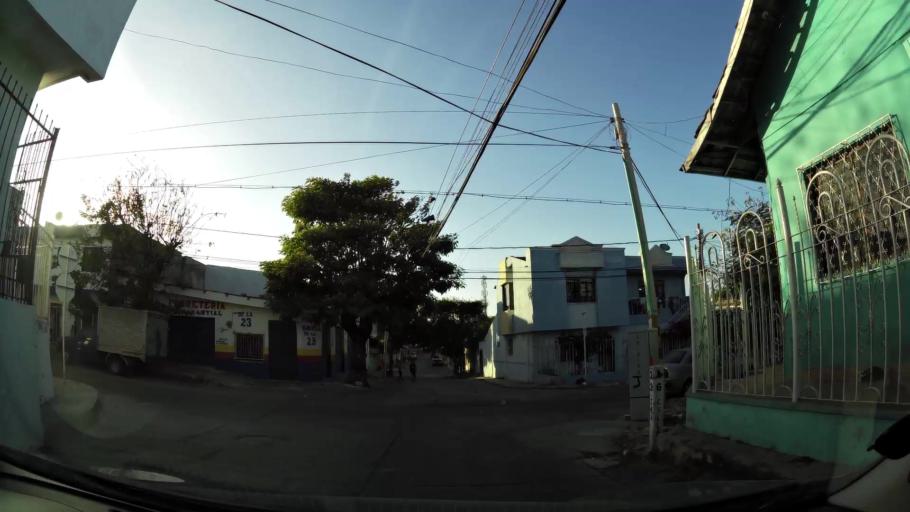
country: CO
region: Atlantico
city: Barranquilla
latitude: 10.9661
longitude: -74.7923
